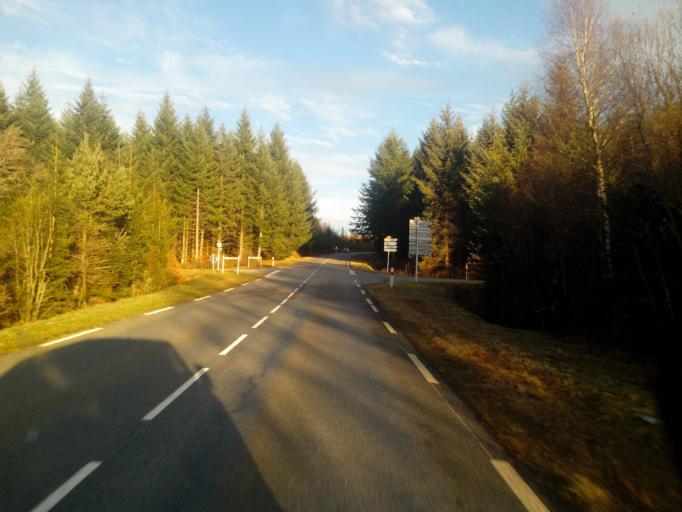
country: FR
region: Limousin
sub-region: Departement de la Correze
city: Bugeat
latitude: 45.5686
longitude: 2.0376
